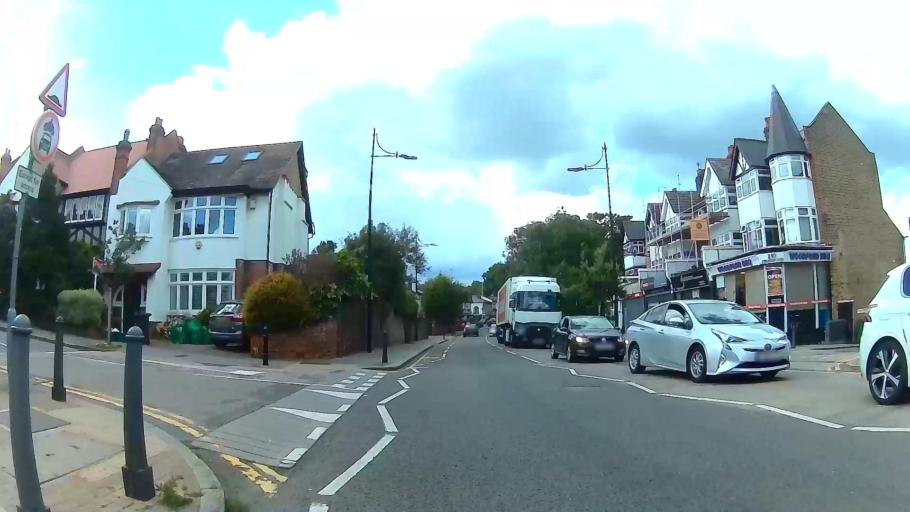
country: GB
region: England
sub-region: Greater London
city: Woodford Green
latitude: 51.6008
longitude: 0.0196
